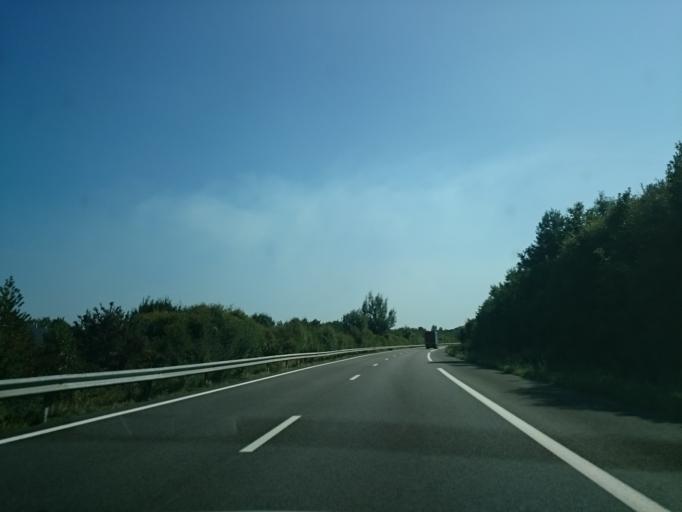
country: FR
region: Pays de la Loire
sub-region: Departement de la Loire-Atlantique
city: Jans
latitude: 47.6066
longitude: -1.6287
